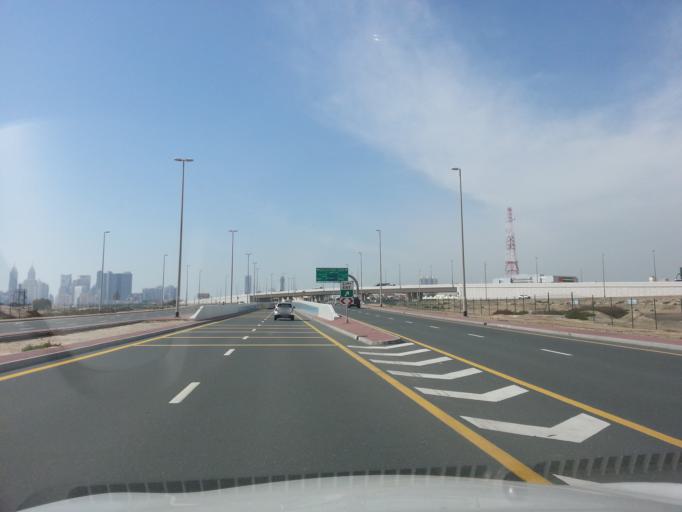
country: AE
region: Dubai
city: Dubai
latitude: 25.0819
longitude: 55.1994
